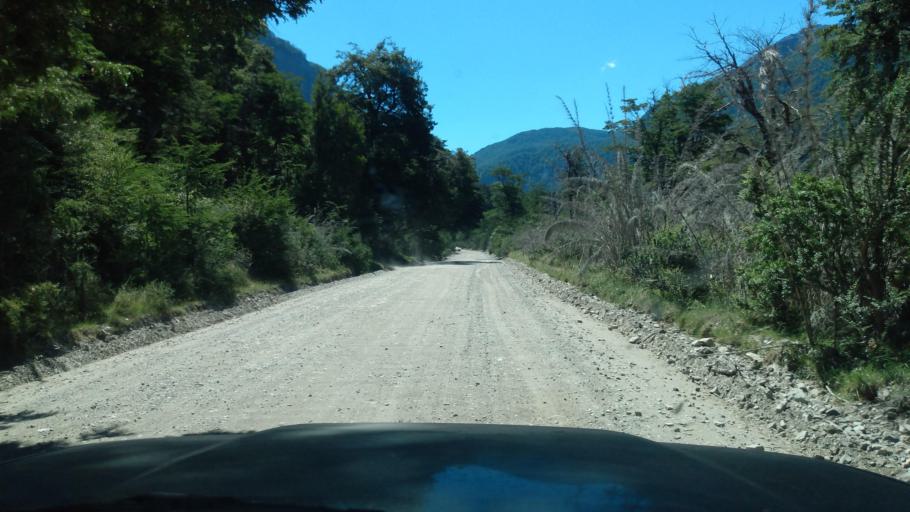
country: AR
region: Neuquen
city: Villa La Angostura
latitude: -40.6192
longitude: -71.6045
